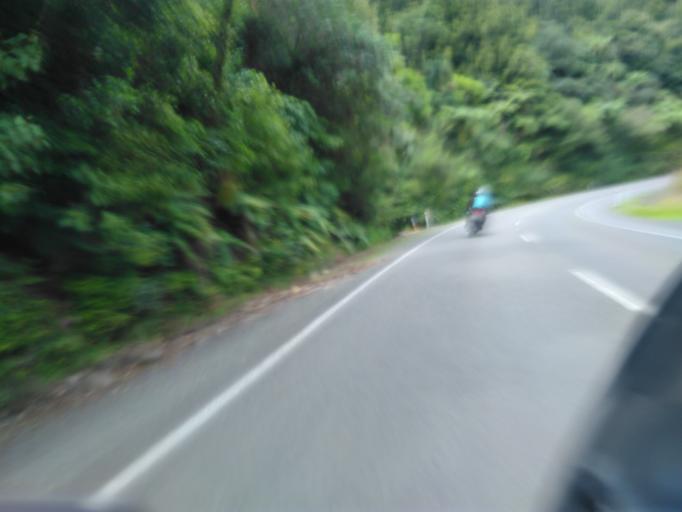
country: NZ
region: Bay of Plenty
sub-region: Opotiki District
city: Opotiki
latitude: -38.2876
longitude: 177.3615
